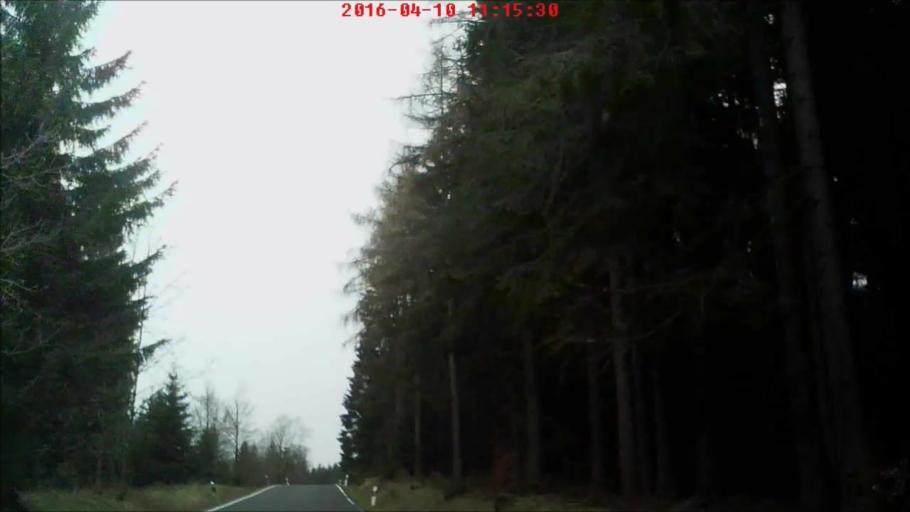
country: DE
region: Thuringia
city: Frauenwald
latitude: 50.5986
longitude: 10.8471
